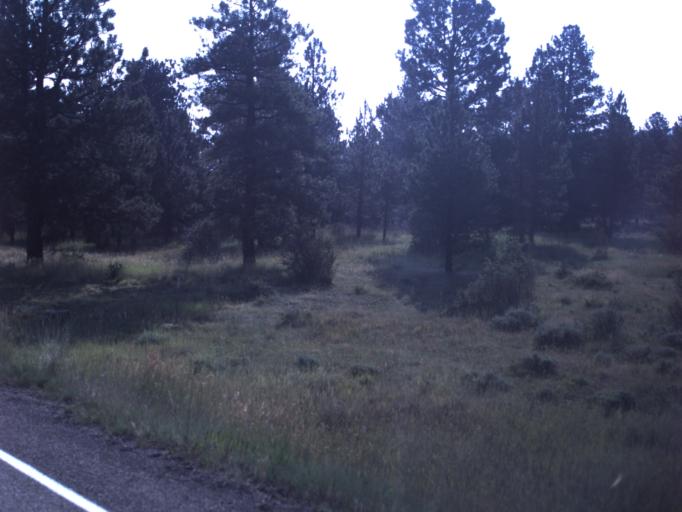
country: US
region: Utah
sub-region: Daggett County
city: Manila
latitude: 40.8653
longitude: -109.4770
